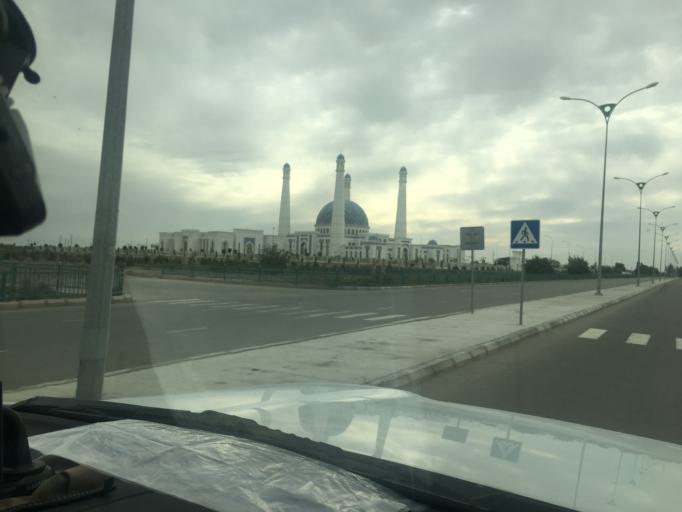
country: TM
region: Dasoguz
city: Dasoguz
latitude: 41.8405
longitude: 59.9157
